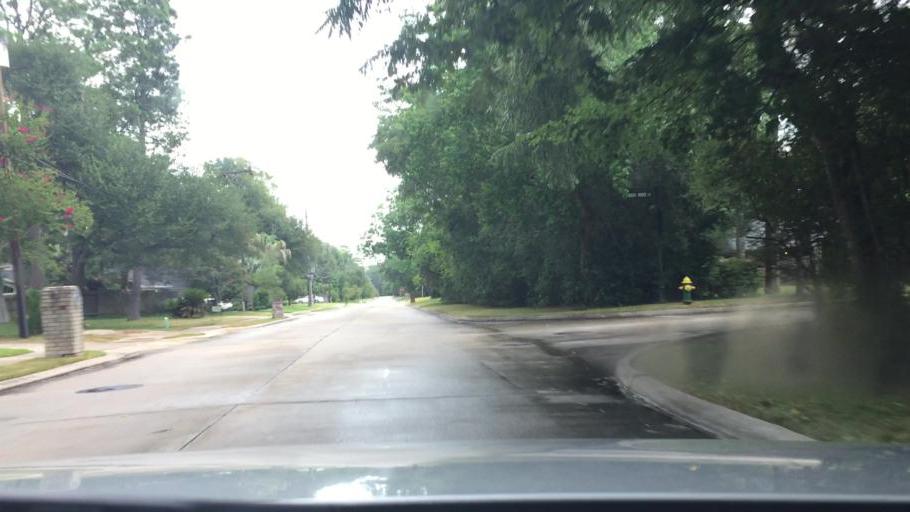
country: US
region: Texas
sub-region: Harris County
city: Piney Point Village
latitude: 29.7664
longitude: -95.5153
